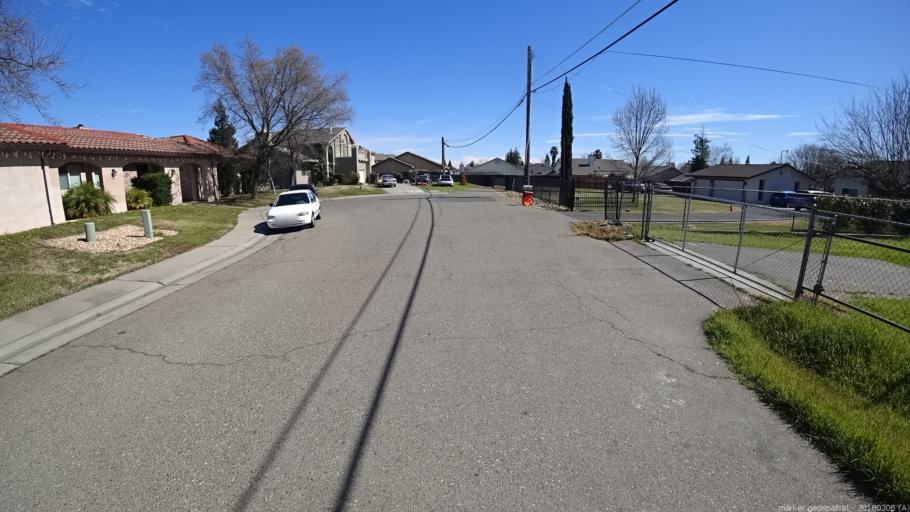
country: US
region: California
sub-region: Sacramento County
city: Vineyard
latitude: 38.4562
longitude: -121.3630
